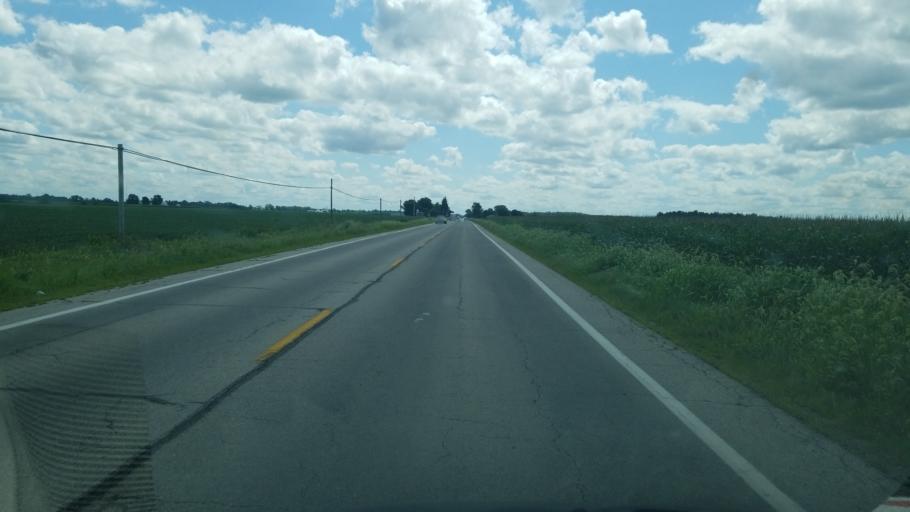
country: US
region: Ohio
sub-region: Henry County
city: Napoleon
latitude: 41.3520
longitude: -84.1197
